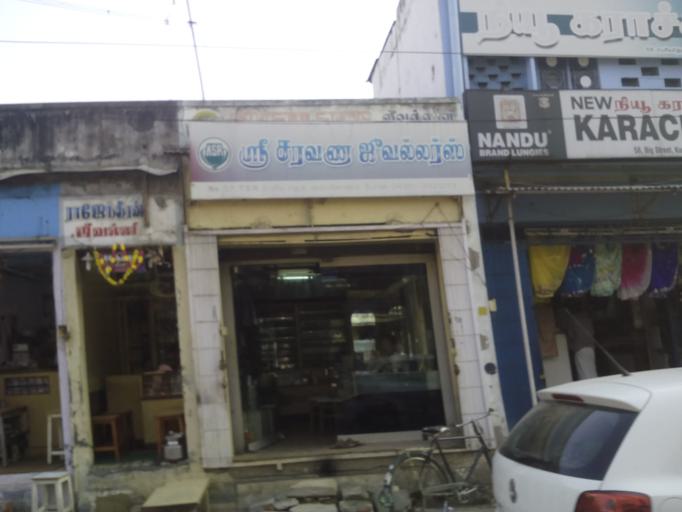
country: IN
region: Tamil Nadu
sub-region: Thanjavur
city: Kumbakonam
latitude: 10.9603
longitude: 79.3739
